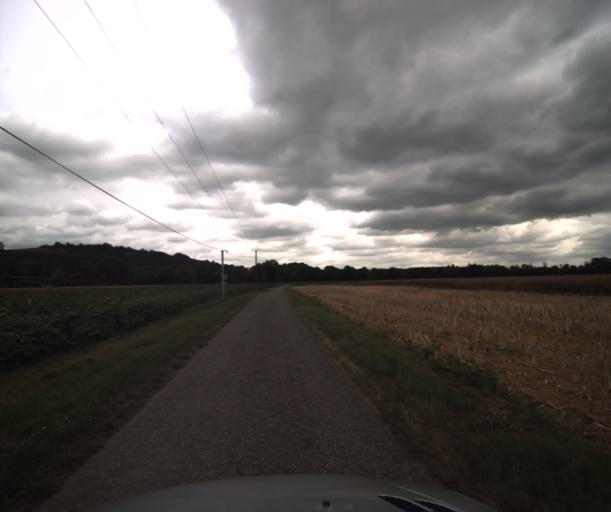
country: FR
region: Midi-Pyrenees
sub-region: Departement de la Haute-Garonne
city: Labarthe-sur-Leze
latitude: 43.4644
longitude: 1.4139
